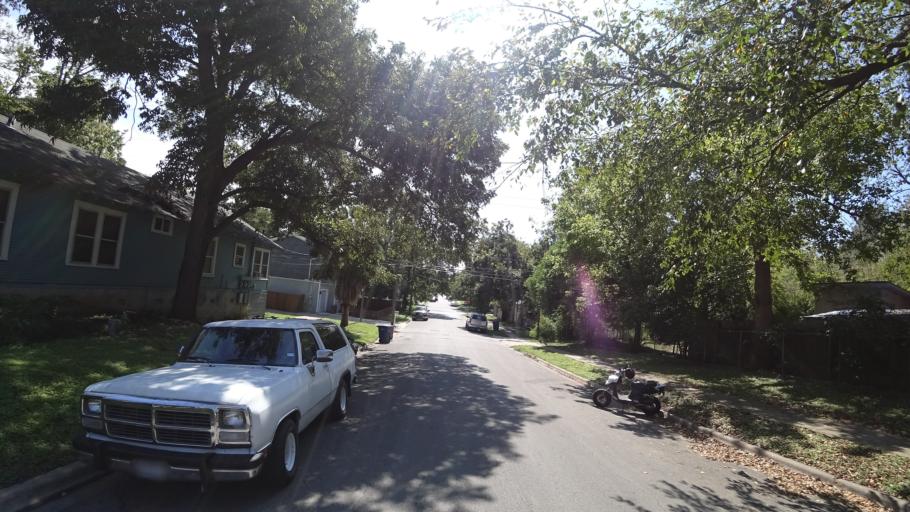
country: US
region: Texas
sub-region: Travis County
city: Austin
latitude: 30.2537
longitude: -97.7247
